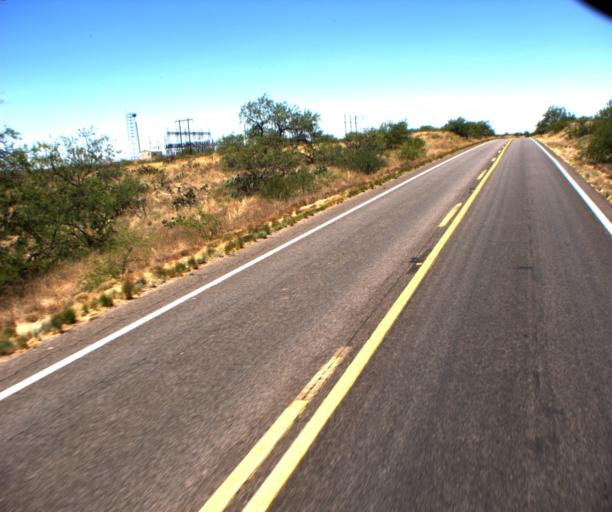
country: US
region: Arizona
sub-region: Pima County
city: Catalina
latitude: 32.6000
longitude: -110.9791
